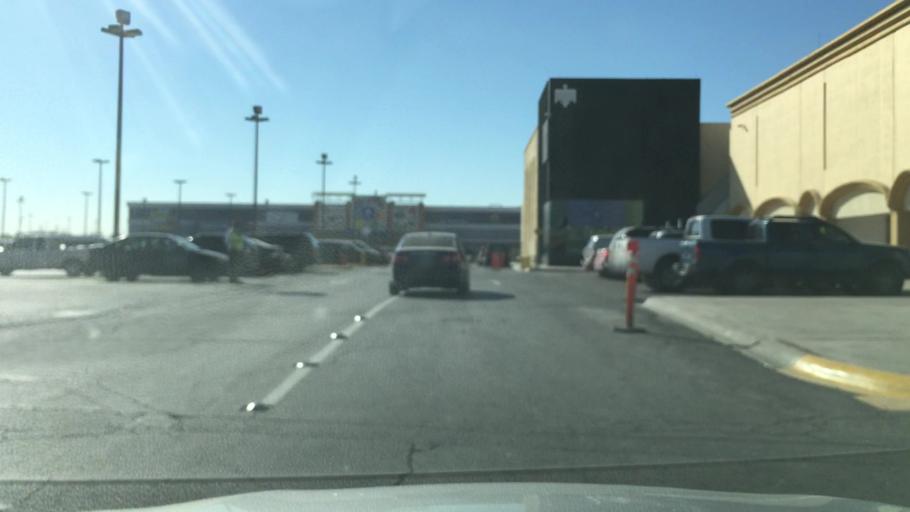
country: MX
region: Chihuahua
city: Ciudad Juarez
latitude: 31.7366
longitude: -106.4461
